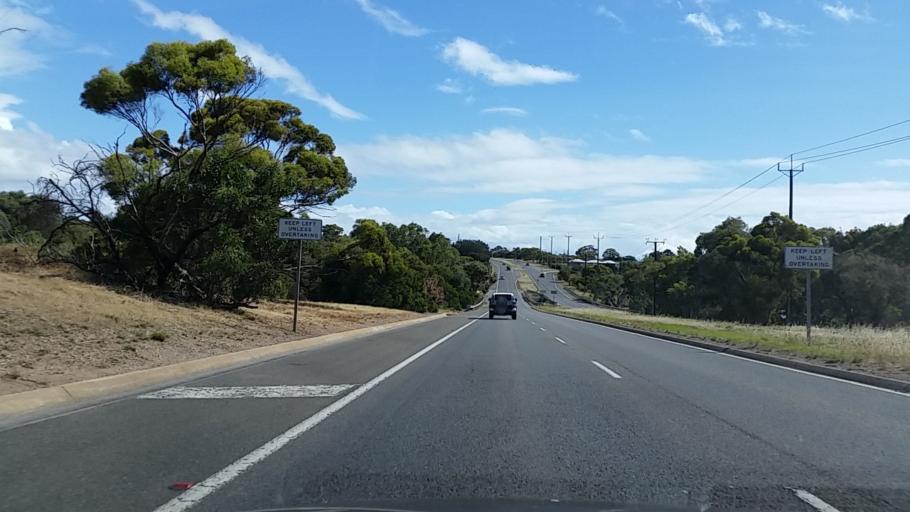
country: AU
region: South Australia
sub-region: Onkaparinga
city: Morphett Vale
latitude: -35.1221
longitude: 138.4879
